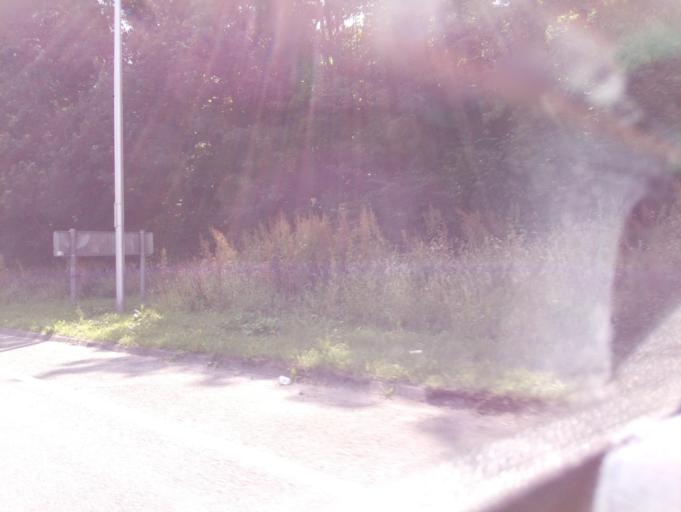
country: GB
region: Wales
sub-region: Caerphilly County Borough
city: Llanbradach
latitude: 51.5959
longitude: -3.2307
